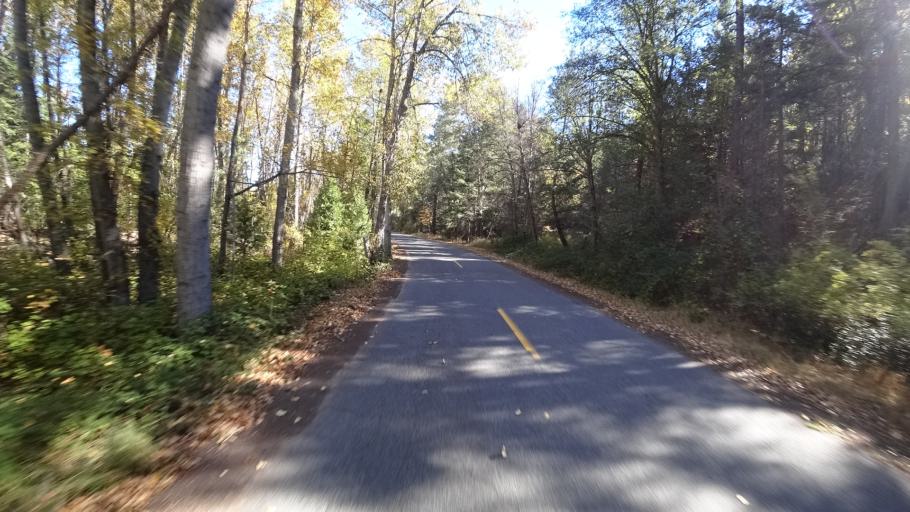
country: US
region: California
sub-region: Siskiyou County
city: Yreka
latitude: 41.5359
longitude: -122.9346
